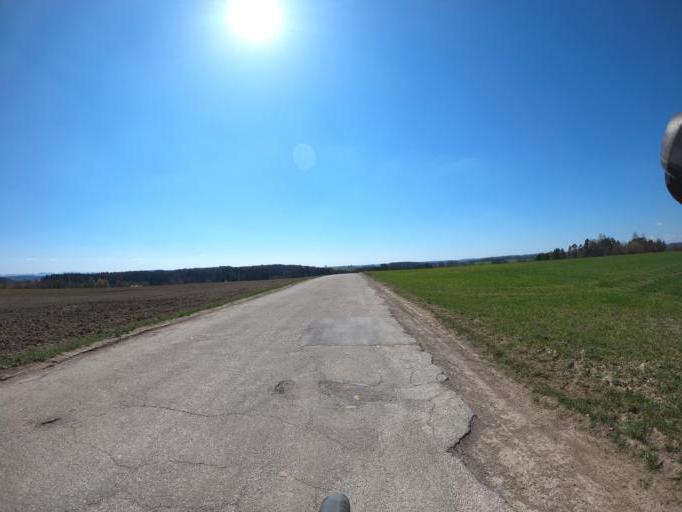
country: DE
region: Baden-Wuerttemberg
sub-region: Karlsruhe Region
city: Horb am Neckar
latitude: 48.4217
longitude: 8.6883
